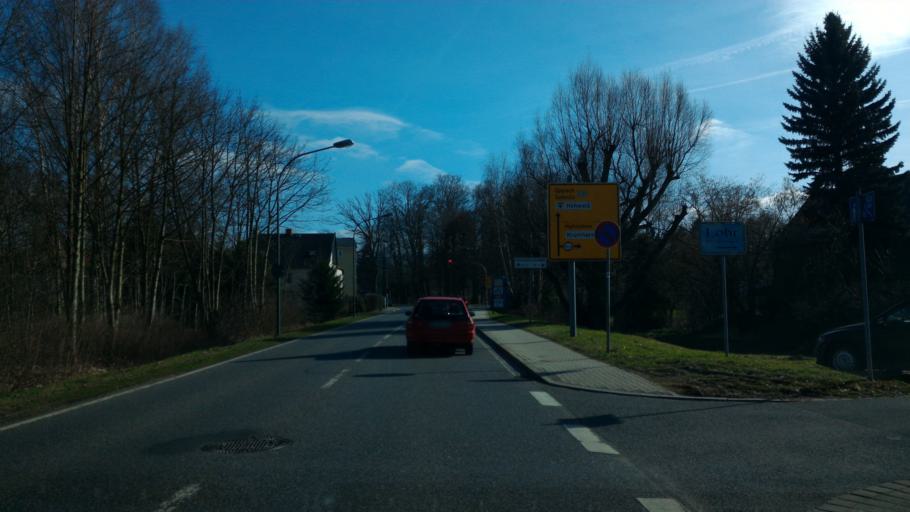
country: DE
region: Saxony
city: Neustadt in Sachsen
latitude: 51.0255
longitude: 14.2195
